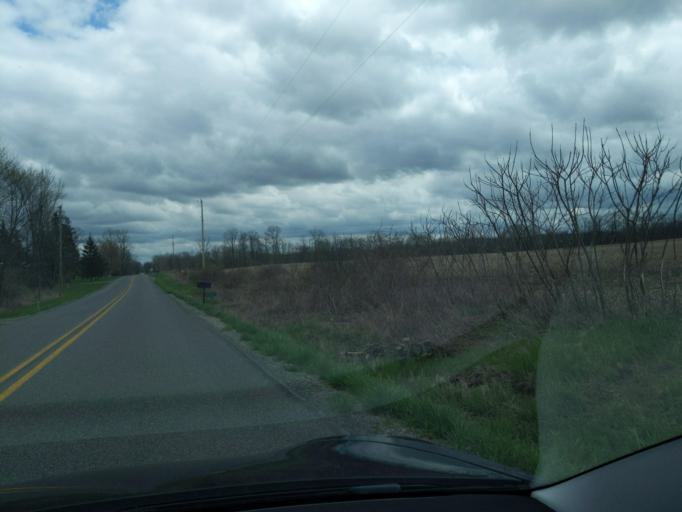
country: US
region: Michigan
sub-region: Eaton County
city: Eaton Rapids
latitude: 42.5676
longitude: -84.5954
